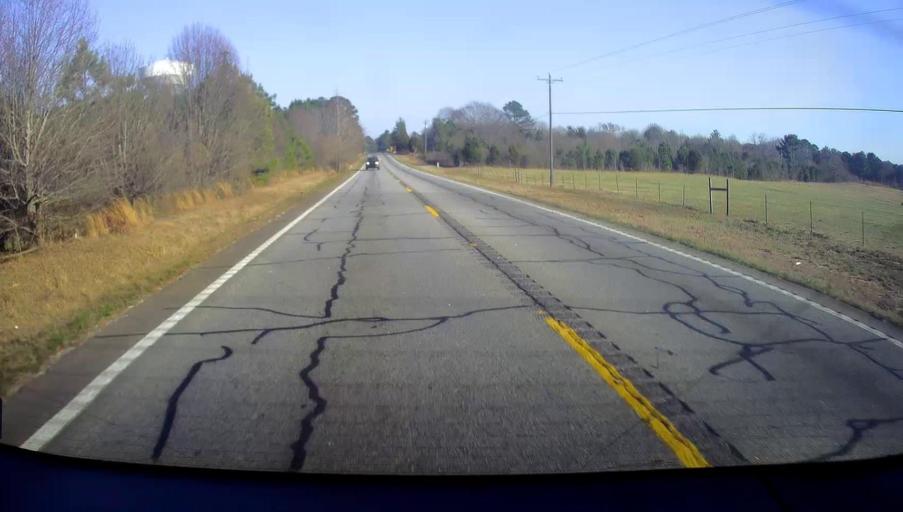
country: US
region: Georgia
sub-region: Henry County
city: Hampton
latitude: 33.4213
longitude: -84.2674
